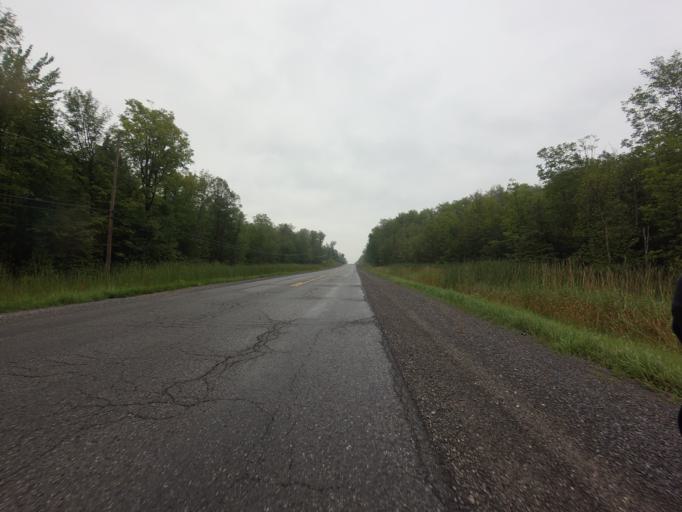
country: CA
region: Ontario
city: Carleton Place
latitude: 45.1492
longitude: -76.3122
